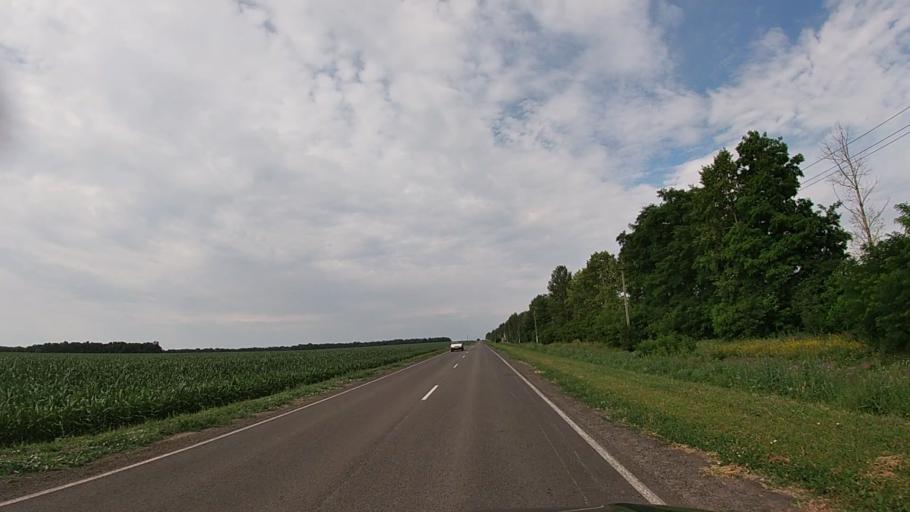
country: RU
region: Belgorod
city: Krasnaya Yaruga
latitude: 50.8265
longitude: 35.4702
